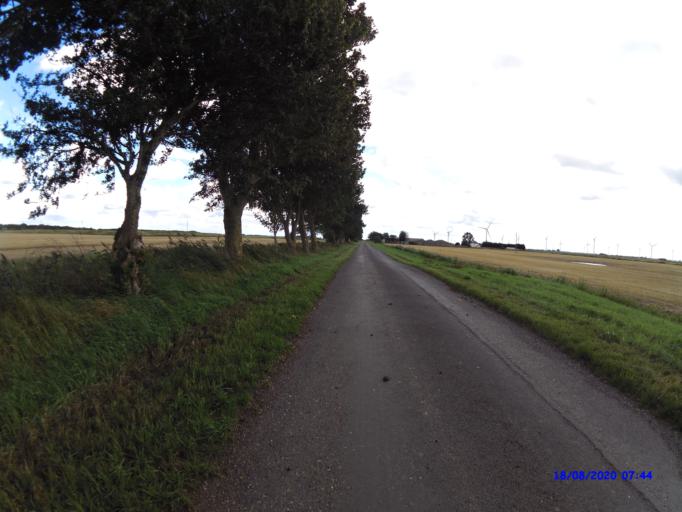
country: GB
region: England
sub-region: Cambridgeshire
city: Whittlesey
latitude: 52.5268
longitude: -0.1035
